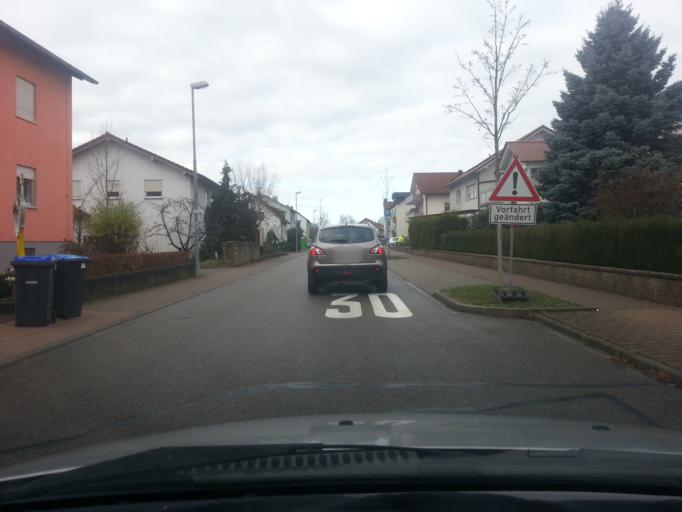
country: DE
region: Baden-Wuerttemberg
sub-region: Regierungsbezirk Stuttgart
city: Eppingen
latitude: 49.1399
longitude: 8.9106
